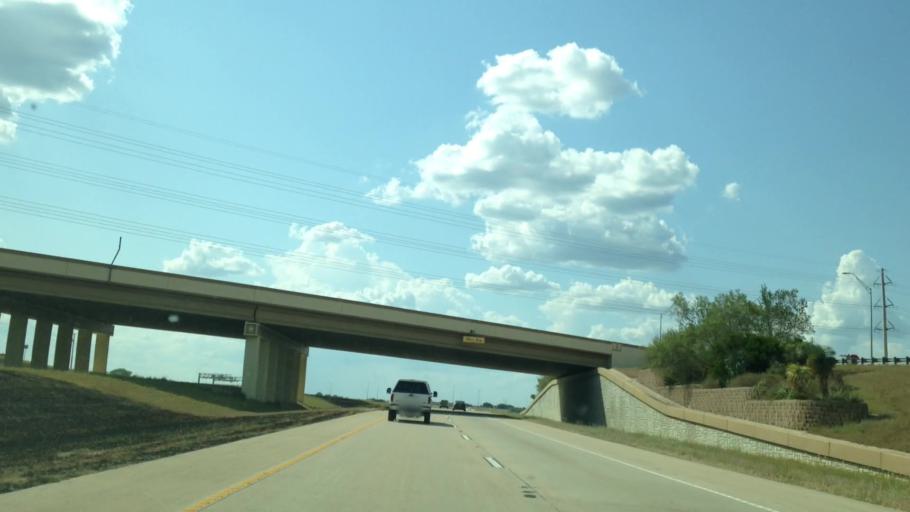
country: US
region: Texas
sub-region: Travis County
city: Onion Creek
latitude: 30.1020
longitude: -97.7806
